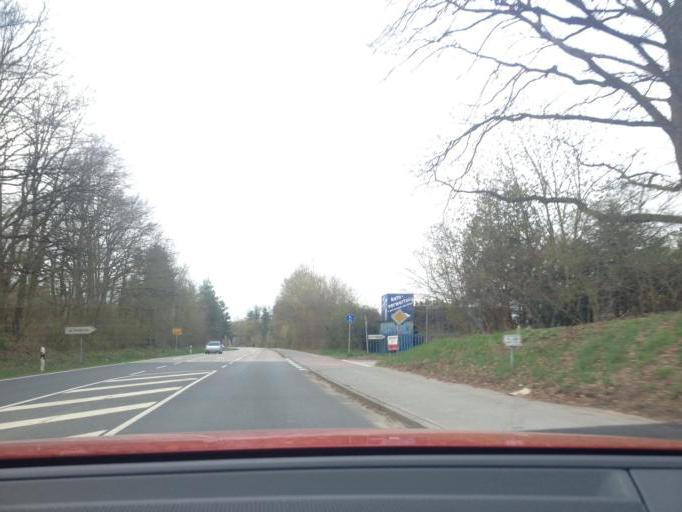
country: DE
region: Bavaria
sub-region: Regierungsbezirk Mittelfranken
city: Ottensoos
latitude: 49.5246
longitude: 11.3395
